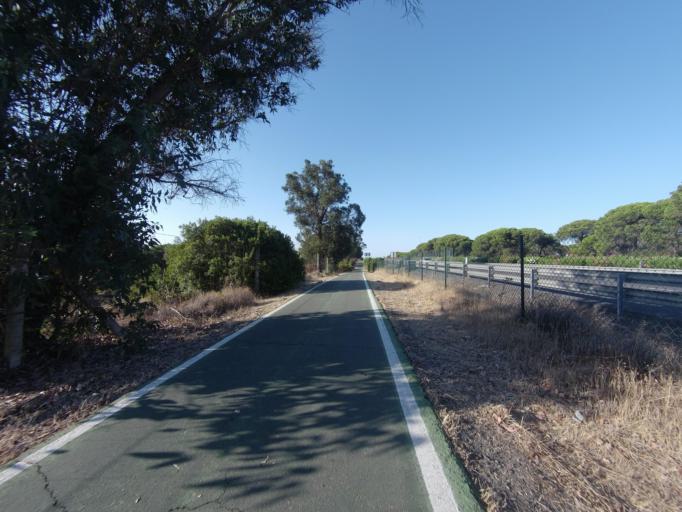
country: ES
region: Andalusia
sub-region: Provincia de Huelva
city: Aljaraque
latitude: 37.2426
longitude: -7.0183
